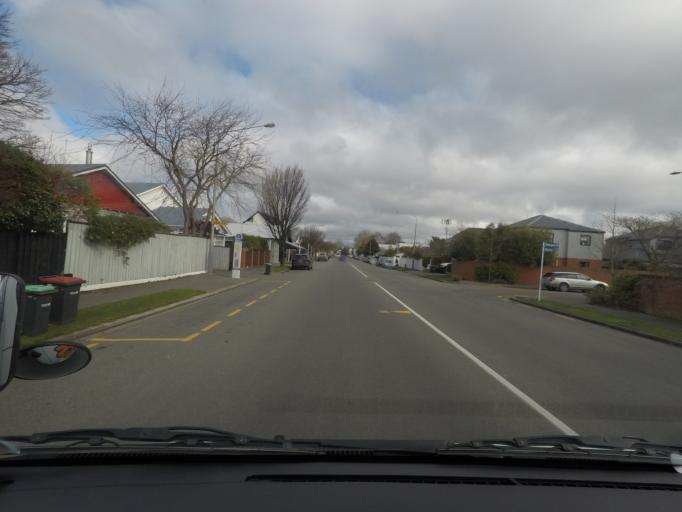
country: NZ
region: Canterbury
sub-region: Christchurch City
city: Christchurch
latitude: -43.5116
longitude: 172.6256
